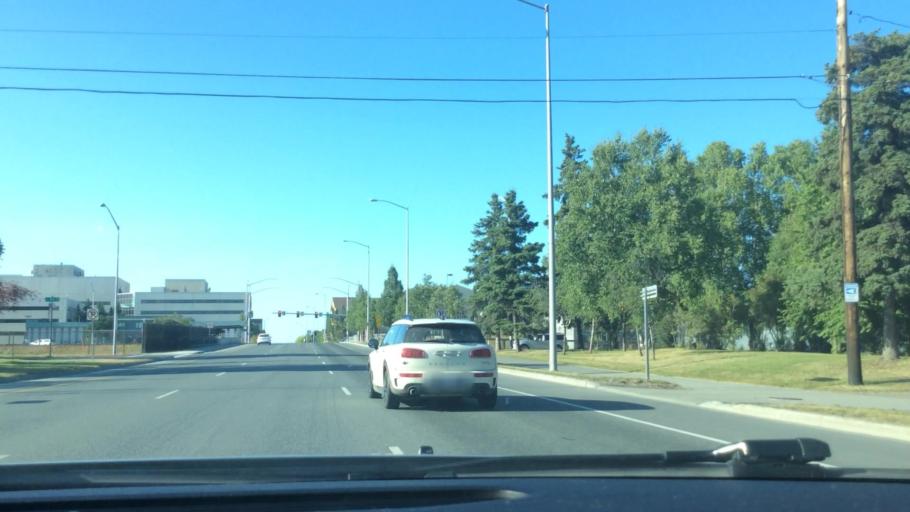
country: US
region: Alaska
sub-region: Anchorage Municipality
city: Anchorage
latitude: 61.2120
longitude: -149.8832
